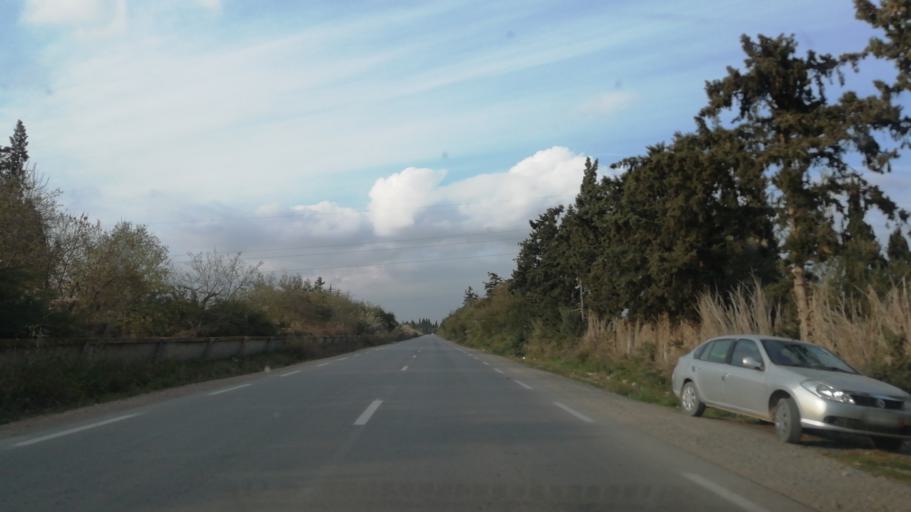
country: DZ
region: Mascara
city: Mascara
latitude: 35.6266
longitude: 0.0428
